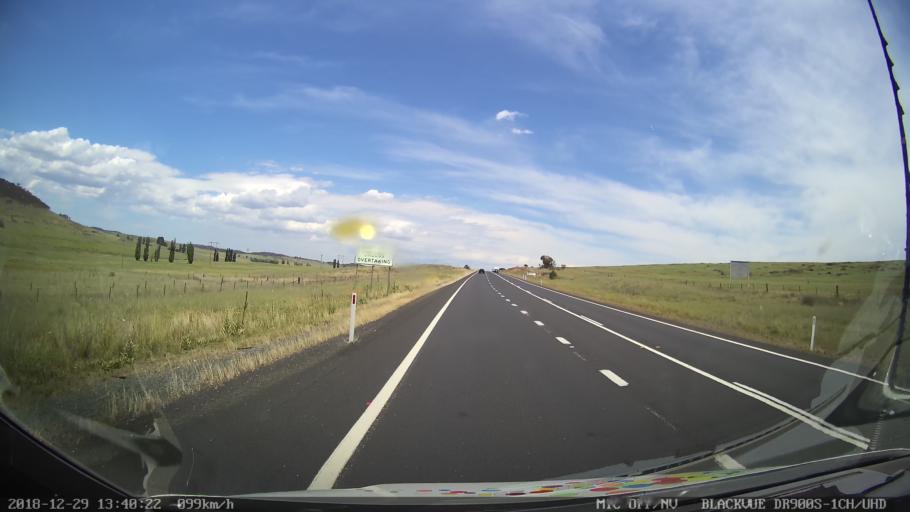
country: AU
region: New South Wales
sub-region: Cooma-Monaro
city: Cooma
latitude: -36.0261
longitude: 149.1517
